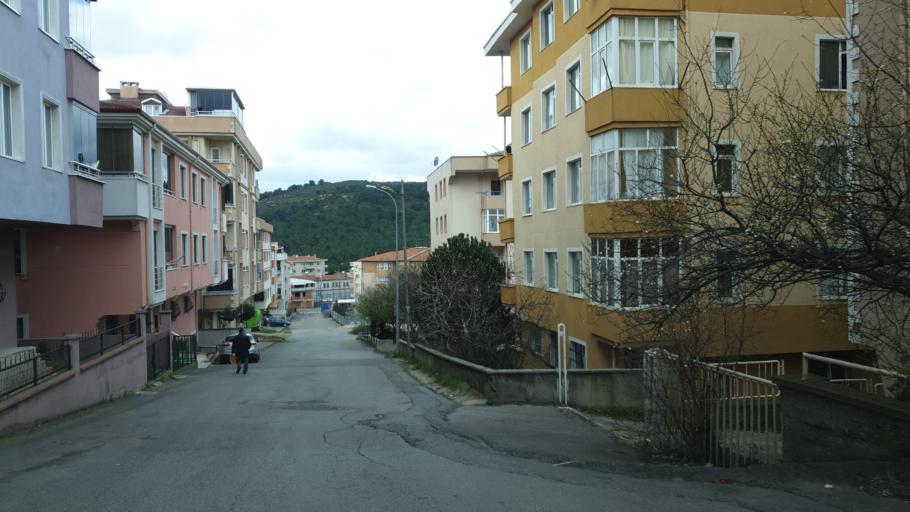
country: TR
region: Istanbul
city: Pendik
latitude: 40.9050
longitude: 29.2478
